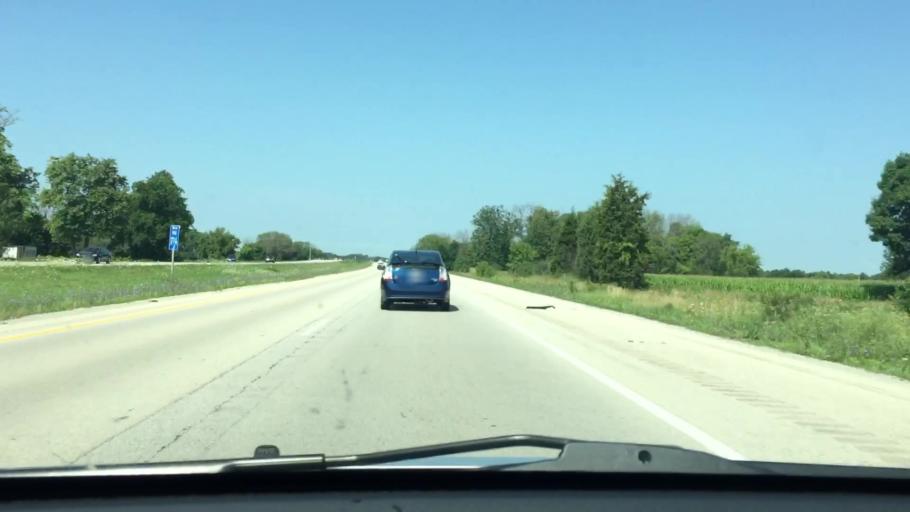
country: US
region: Wisconsin
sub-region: Waukesha County
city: Oconomowoc
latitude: 43.0706
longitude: -88.5495
